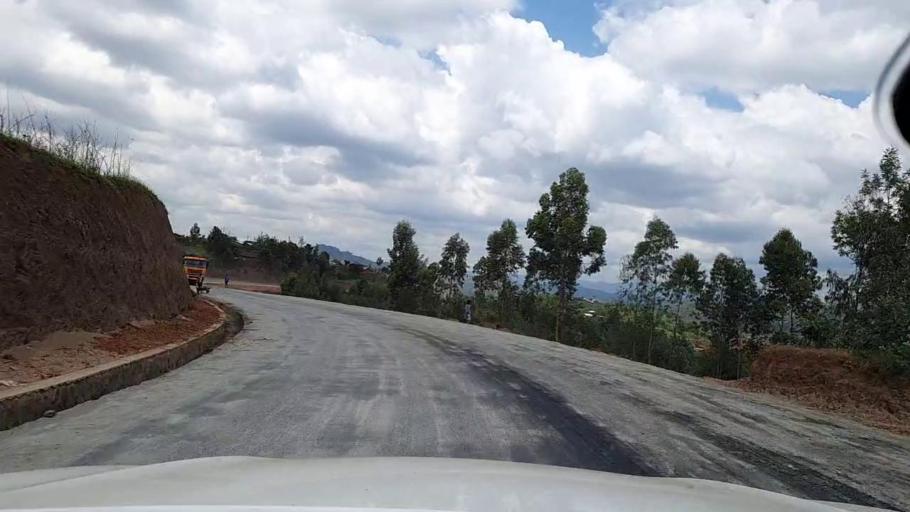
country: RW
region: Southern Province
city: Butare
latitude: -2.6979
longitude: 29.5668
